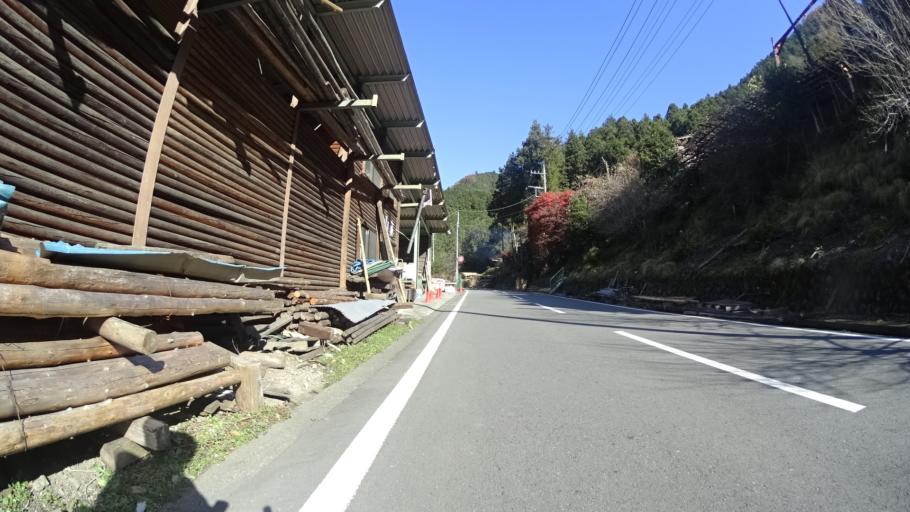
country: JP
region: Saitama
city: Chichibu
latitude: 35.9218
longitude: 139.1520
